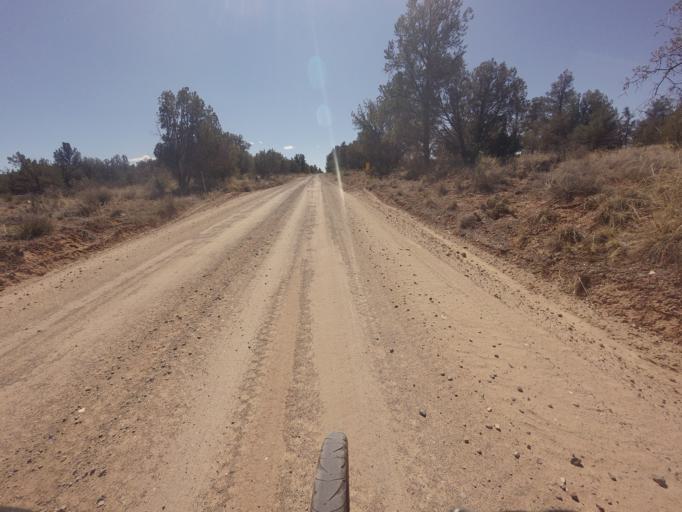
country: US
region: Arizona
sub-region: Yavapai County
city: Lake Montezuma
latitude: 34.6126
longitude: -111.7250
